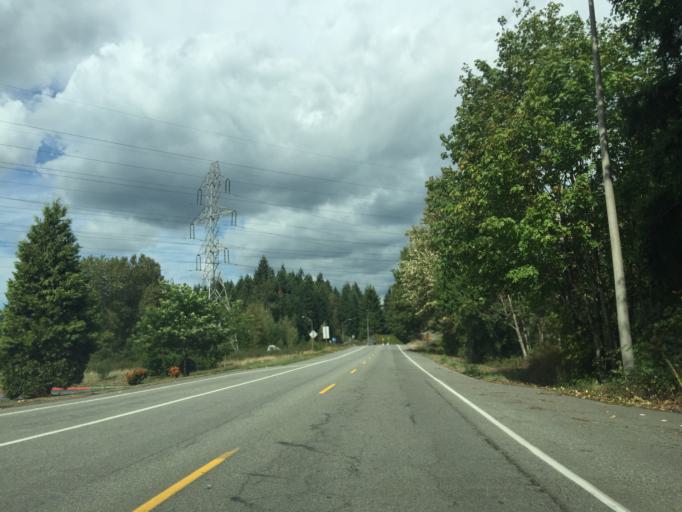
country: US
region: Washington
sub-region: Snohomish County
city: Snohomish
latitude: 47.9317
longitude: -122.1003
